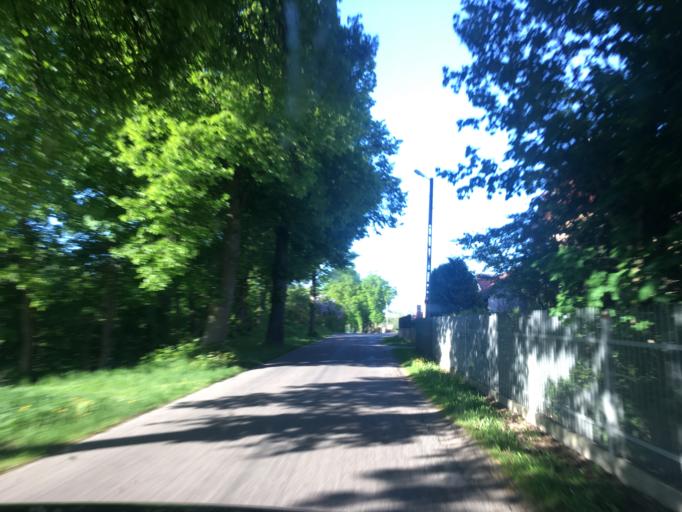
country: PL
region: Warmian-Masurian Voivodeship
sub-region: Powiat piski
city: Ruciane-Nida
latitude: 53.6805
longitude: 21.4966
